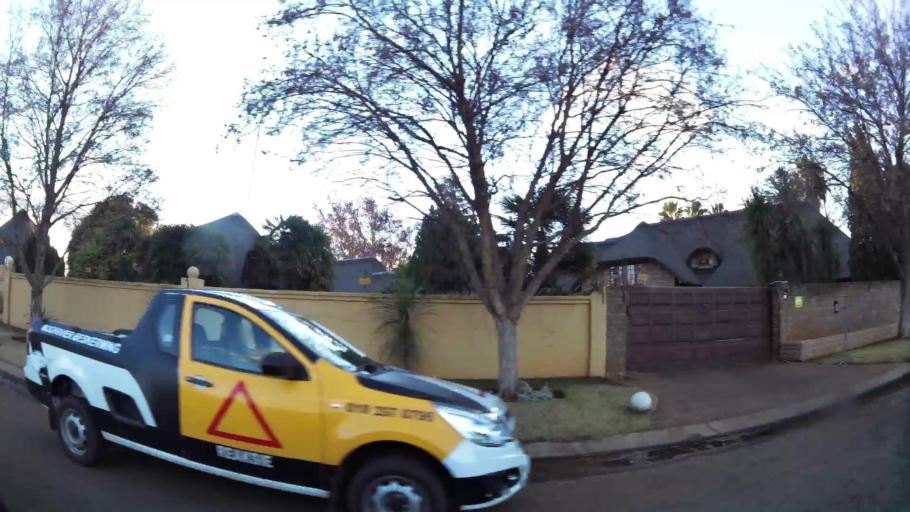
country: ZA
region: North-West
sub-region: Dr Kenneth Kaunda District Municipality
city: Potchefstroom
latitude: -26.6787
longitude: 27.1112
